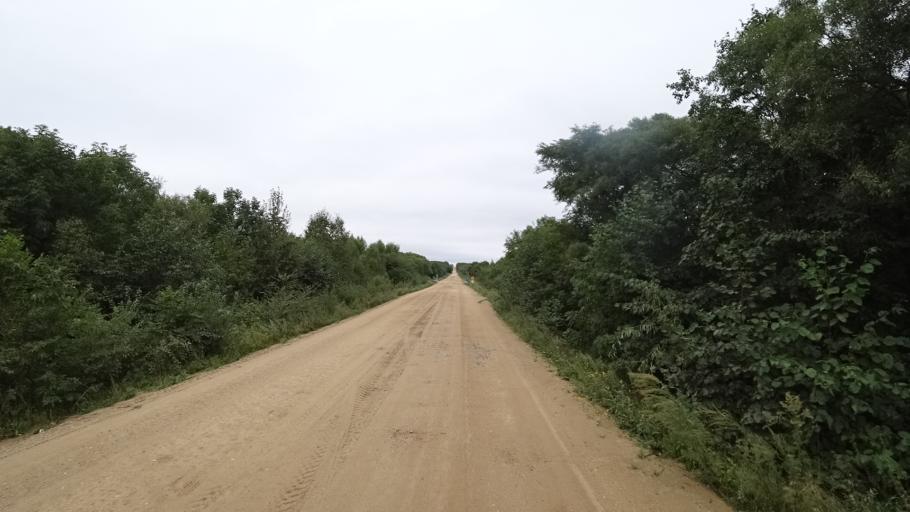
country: RU
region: Primorskiy
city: Ivanovka
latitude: 44.0675
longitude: 132.5757
